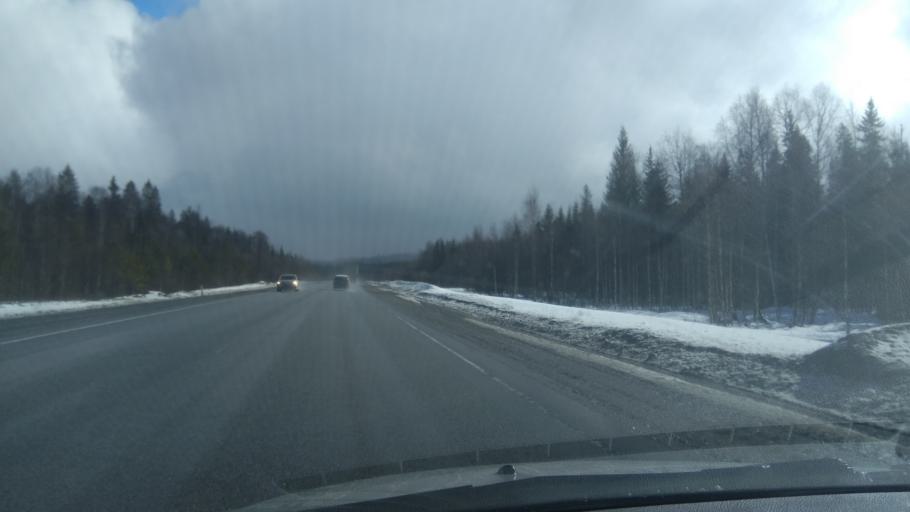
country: RU
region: Sverdlovsk
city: Arti
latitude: 56.7934
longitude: 58.4913
